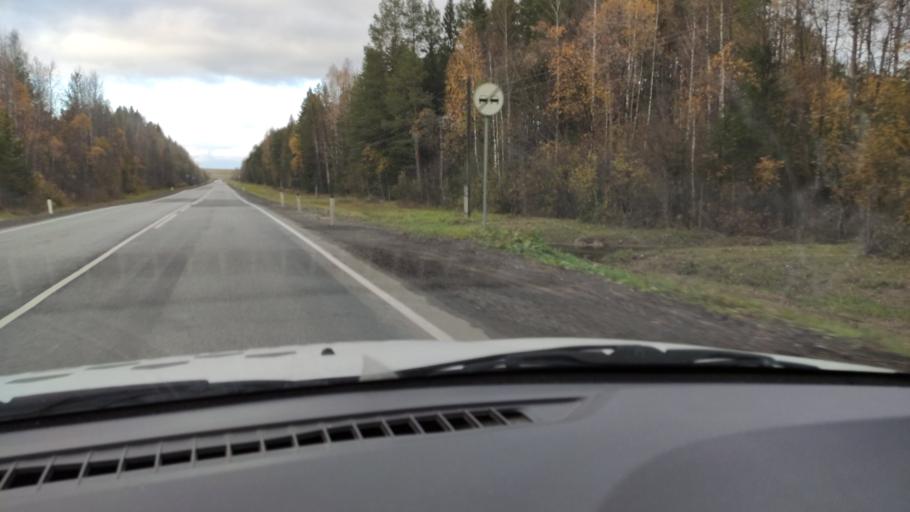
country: RU
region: Kirov
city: Belaya Kholunitsa
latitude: 58.8807
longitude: 50.8718
